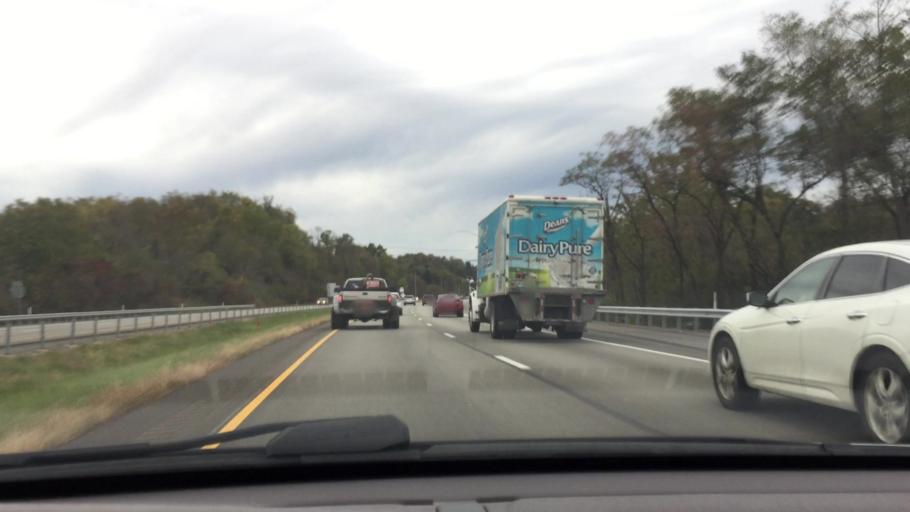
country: US
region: Pennsylvania
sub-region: Beaver County
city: Ambridge
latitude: 40.5531
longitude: -80.2779
